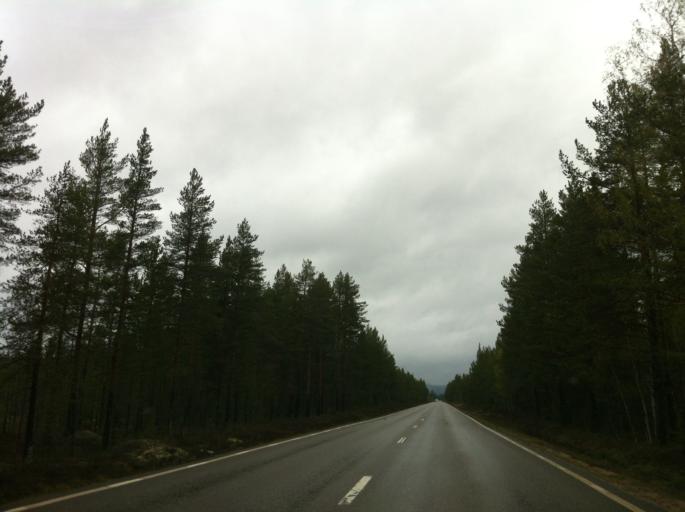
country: SE
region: Jaemtland
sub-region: Harjedalens Kommun
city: Sveg
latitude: 62.1350
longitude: 14.0047
